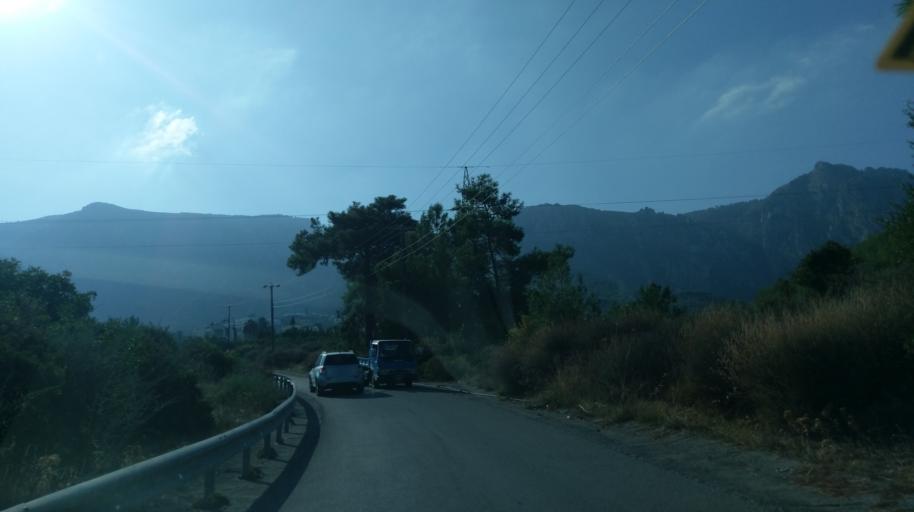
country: CY
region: Keryneia
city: Kyrenia
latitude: 35.3272
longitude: 33.2579
